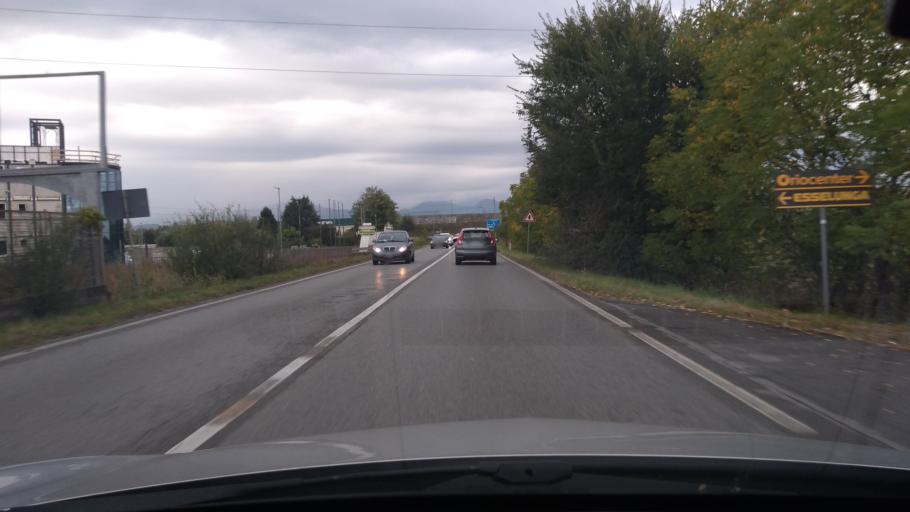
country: IT
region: Lombardy
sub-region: Provincia di Bergamo
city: Stezzano
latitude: 45.6350
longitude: 9.6439
